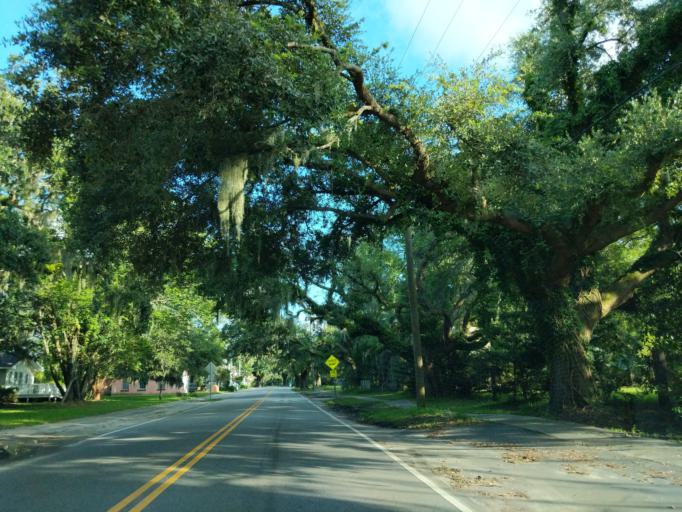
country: US
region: South Carolina
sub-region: Charleston County
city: Awendaw
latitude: 33.0912
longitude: -79.4634
